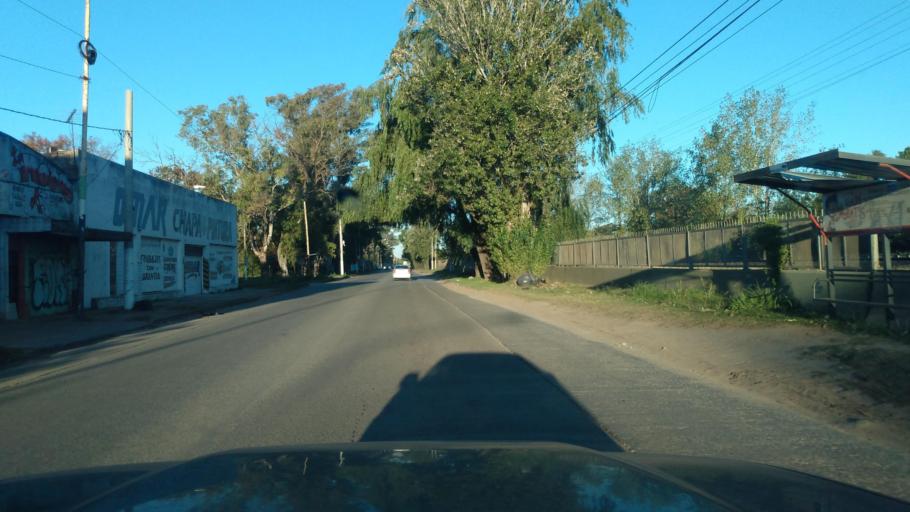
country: AR
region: Buenos Aires
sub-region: Partido de Merlo
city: Merlo
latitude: -34.6449
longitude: -58.8094
